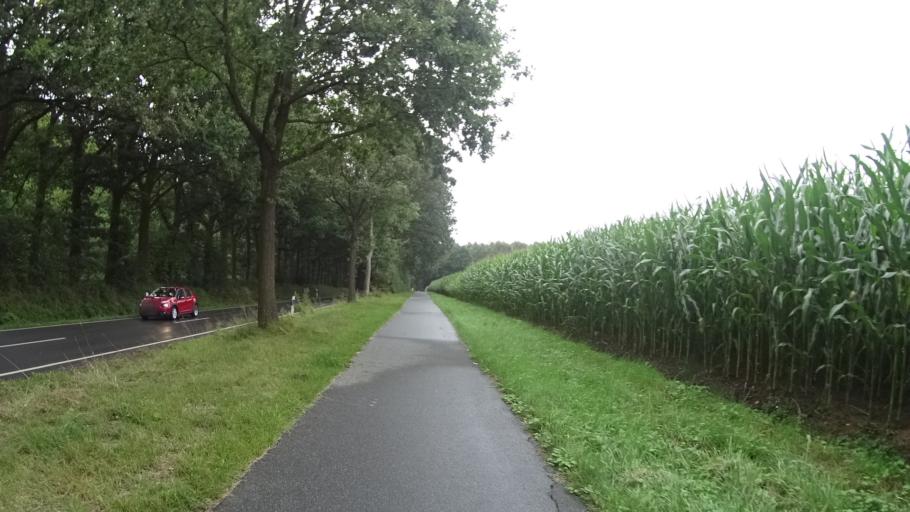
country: DE
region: Schleswig-Holstein
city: Alveslohe
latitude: 53.7830
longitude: 9.9480
